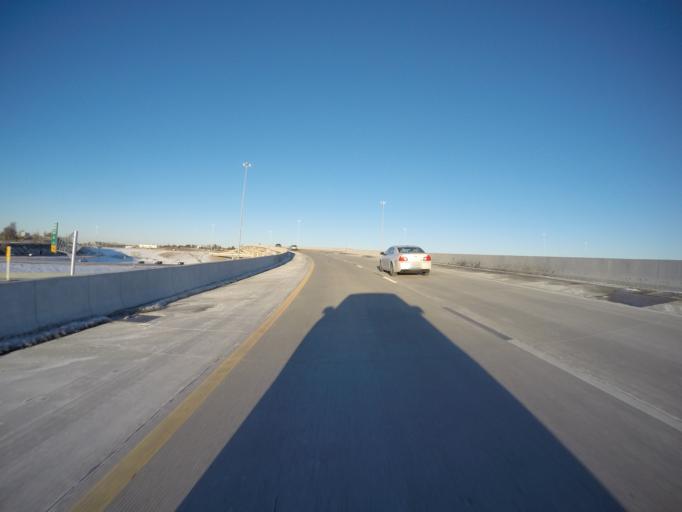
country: US
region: Kansas
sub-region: Johnson County
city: Lenexa
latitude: 38.9423
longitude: -94.7741
